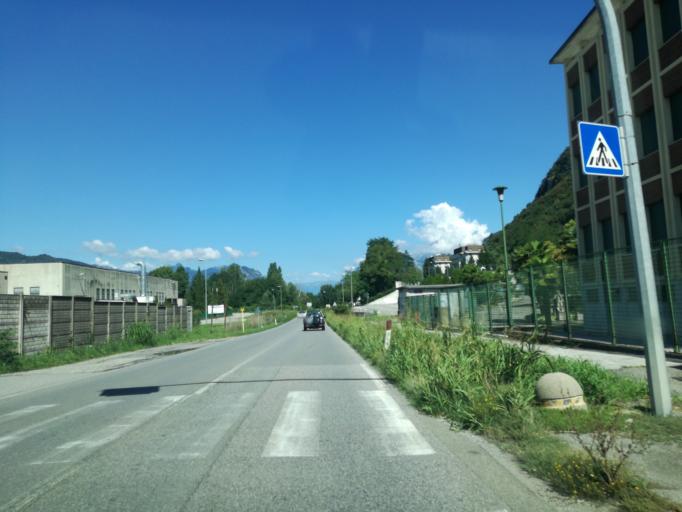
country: IT
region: Lombardy
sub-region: Provincia di Lecco
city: Monte Marenzo
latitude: 45.7638
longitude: 9.4473
